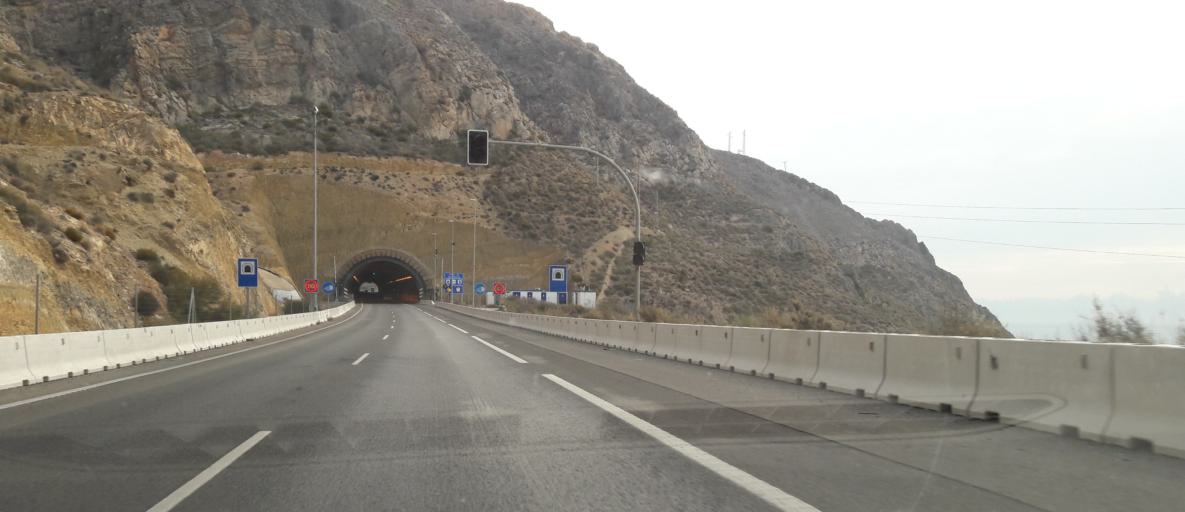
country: ES
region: Andalusia
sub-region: Provincia de Almeria
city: Aguadulce
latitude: 36.8208
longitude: -2.5656
